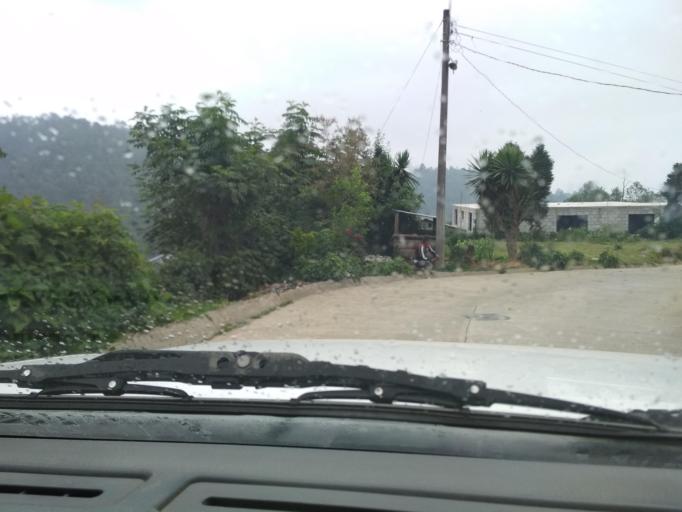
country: MX
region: Veracruz
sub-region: La Perla
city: Chilapa
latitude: 18.9889
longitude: -97.1464
